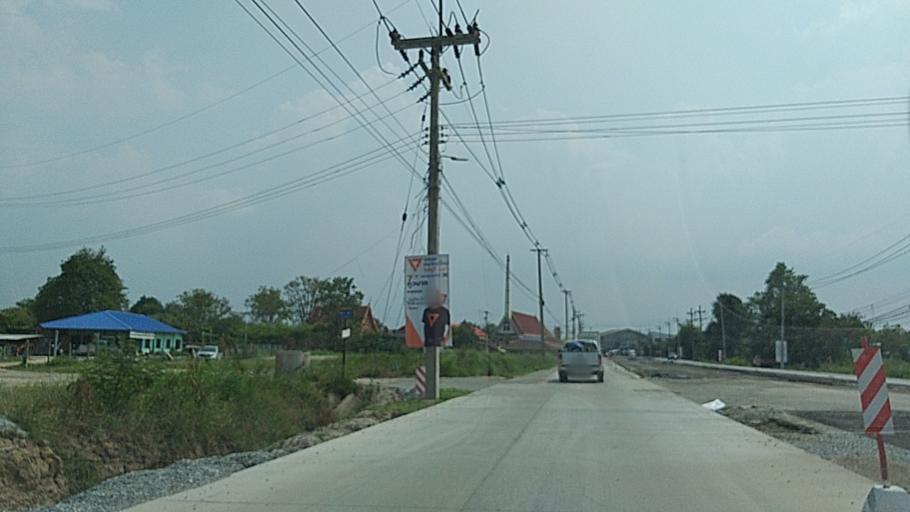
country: TH
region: Chon Buri
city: Phanat Nikhom
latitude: 13.4014
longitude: 101.1904
